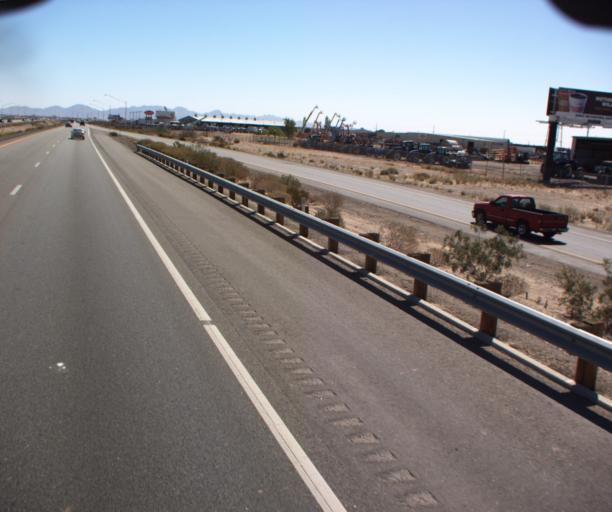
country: US
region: Arizona
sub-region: Yuma County
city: Yuma
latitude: 32.6886
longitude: -114.5793
